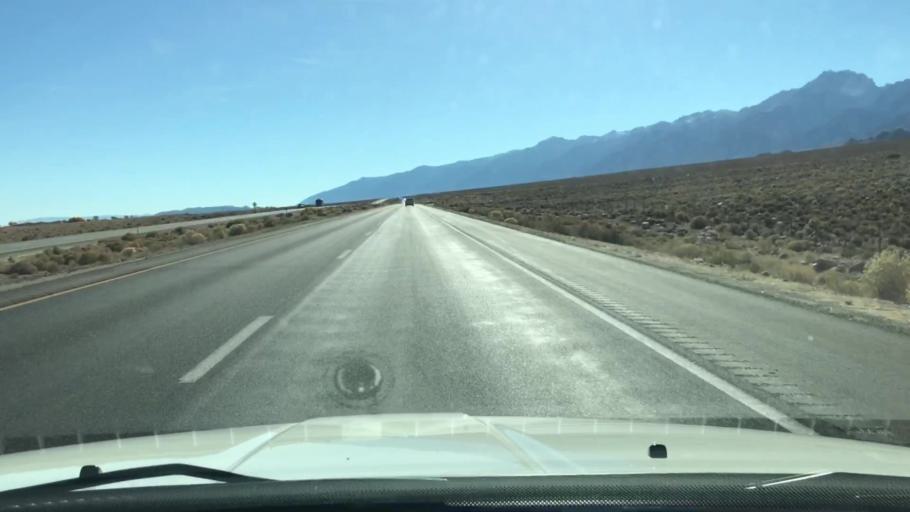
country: US
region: California
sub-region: Inyo County
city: Big Pine
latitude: 36.8703
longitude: -118.2372
